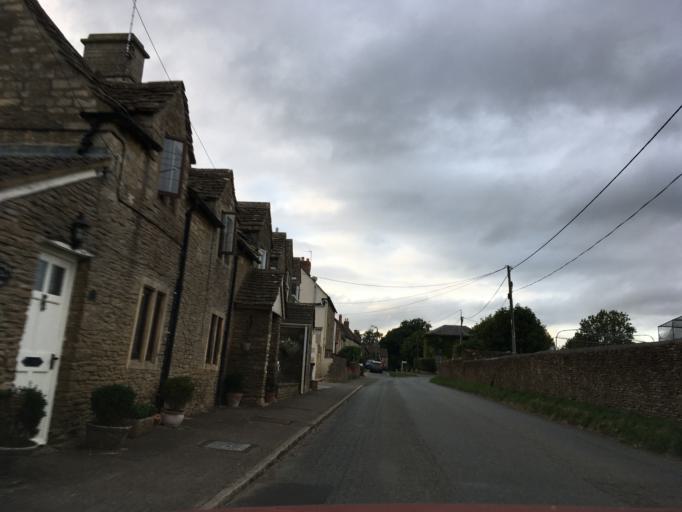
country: GB
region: England
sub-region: Wiltshire
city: Biddestone
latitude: 51.4627
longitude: -2.1995
